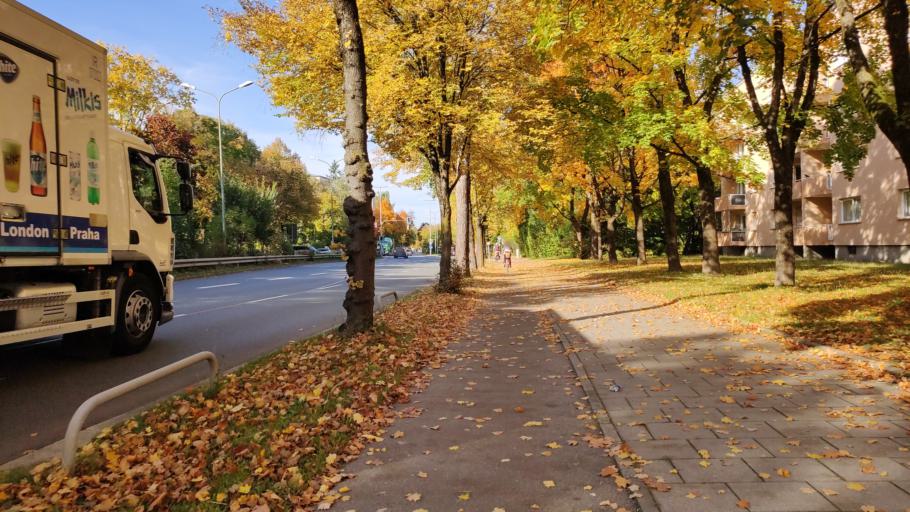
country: DE
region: Bavaria
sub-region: Upper Bavaria
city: Pasing
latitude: 48.1249
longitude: 11.4796
